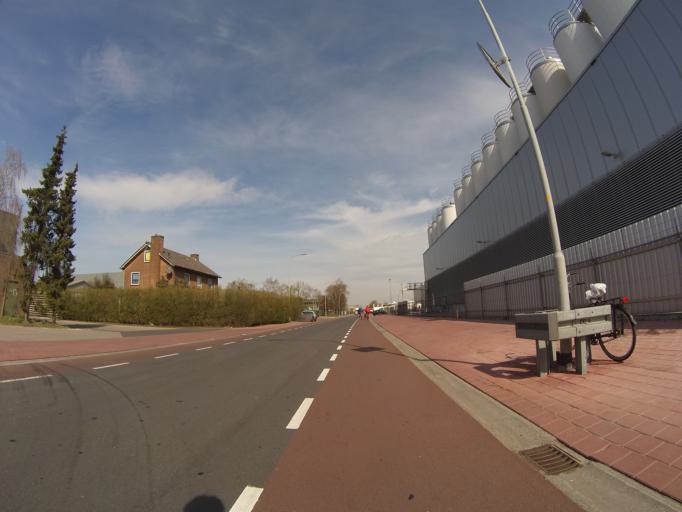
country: NL
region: Gelderland
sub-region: Gemeente Nijkerk
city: Nijkerk
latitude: 52.2353
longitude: 5.4763
